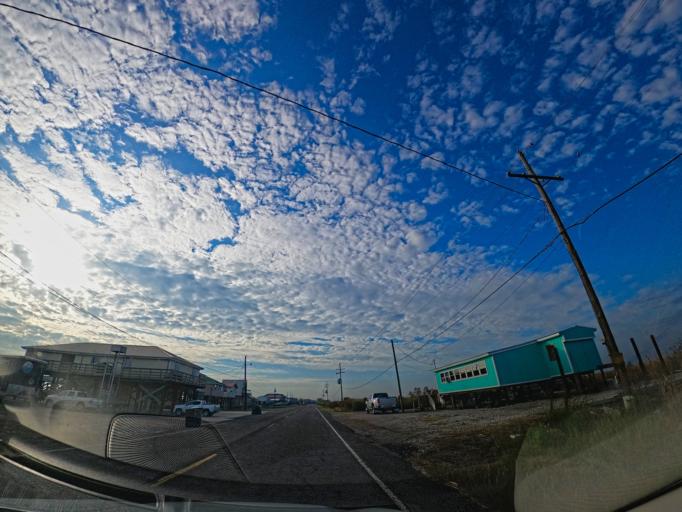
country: US
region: Louisiana
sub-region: Terrebonne Parish
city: Dulac
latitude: 29.2864
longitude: -90.6468
